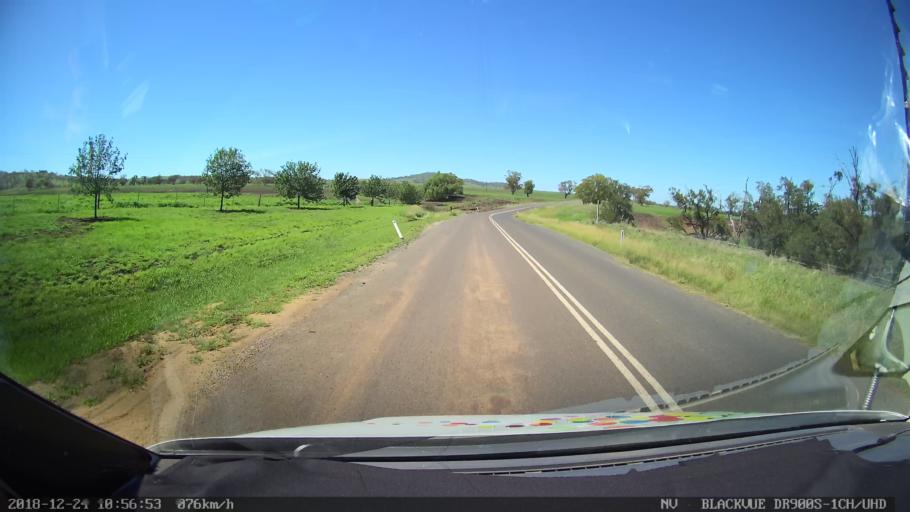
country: AU
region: New South Wales
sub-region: Upper Hunter Shire
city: Merriwa
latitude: -32.0304
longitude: 150.4168
